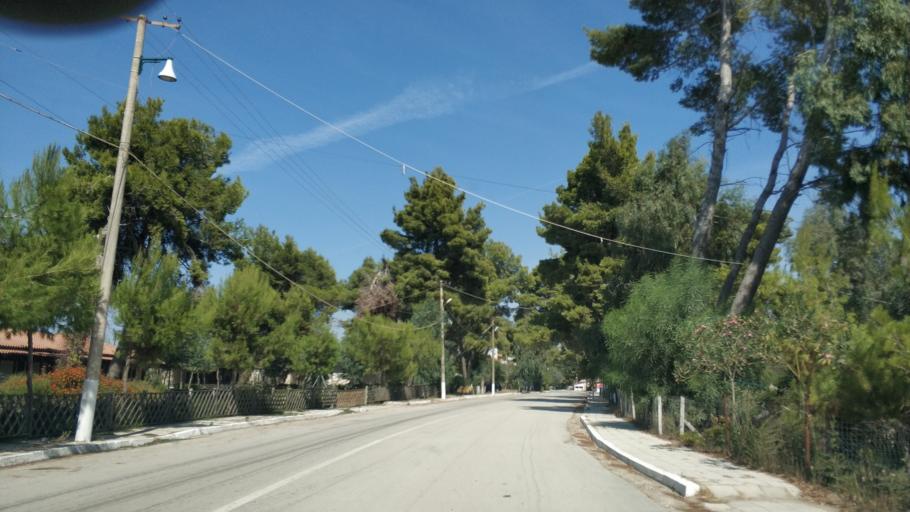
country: AL
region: Fier
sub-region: Rrethi i Lushnjes
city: Divjake
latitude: 40.9683
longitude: 19.4787
